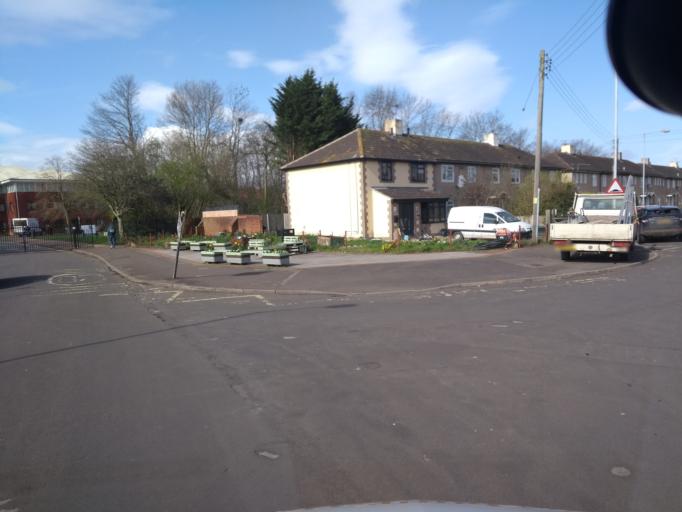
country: GB
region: England
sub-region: Somerset
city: Bridgwater
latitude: 51.1307
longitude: -2.9847
